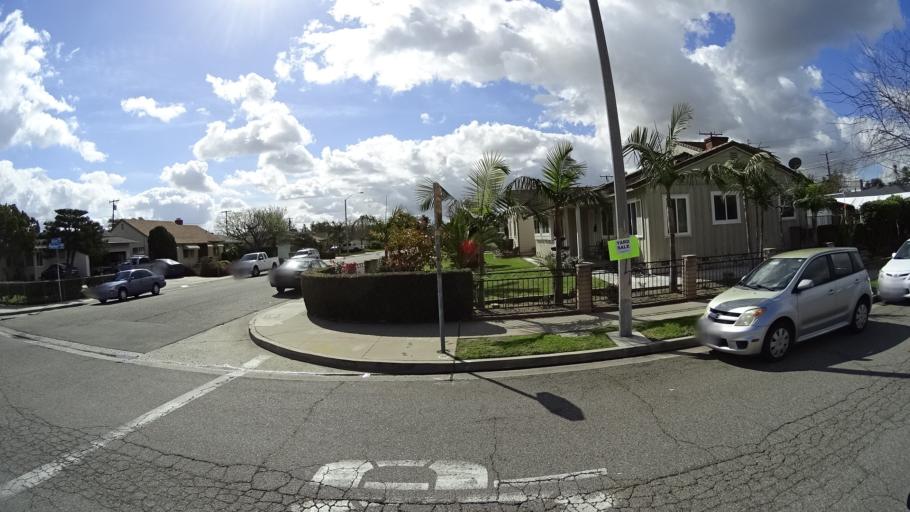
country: US
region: California
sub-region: Orange County
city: Anaheim
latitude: 33.8459
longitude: -117.9012
